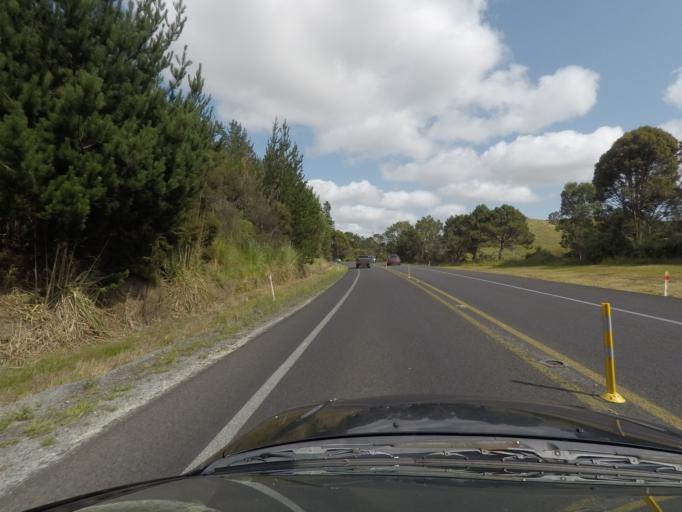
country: NZ
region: Northland
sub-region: Whangarei
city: Whangarei
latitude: -35.8265
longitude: 174.3113
